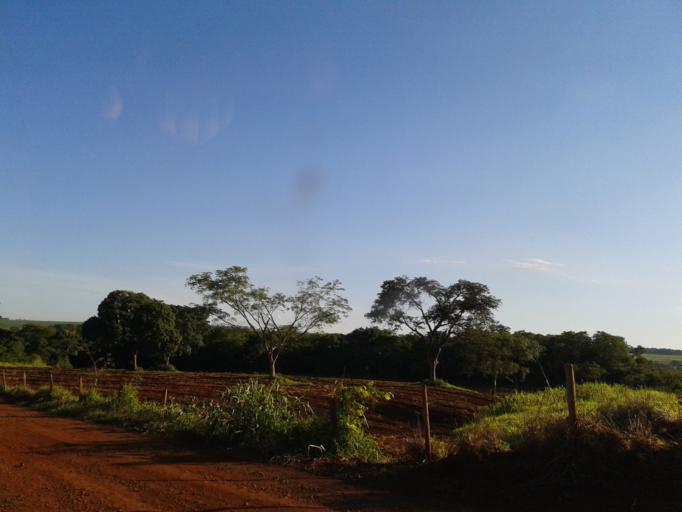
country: BR
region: Minas Gerais
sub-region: Centralina
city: Centralina
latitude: -18.7001
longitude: -49.2788
